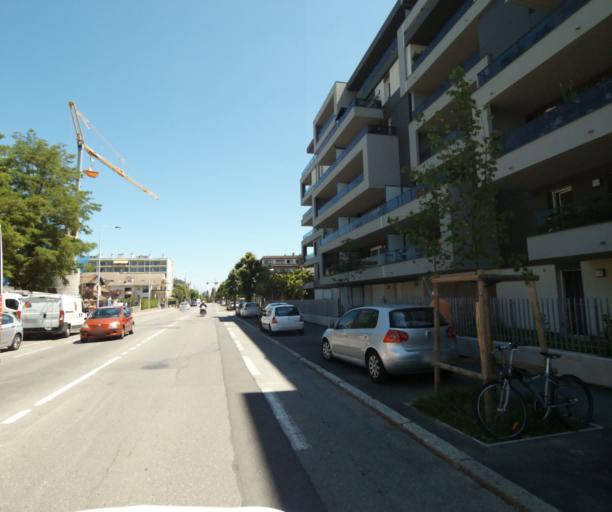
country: FR
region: Rhone-Alpes
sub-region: Departement de la Haute-Savoie
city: Thonon-les-Bains
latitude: 46.3738
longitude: 6.4853
